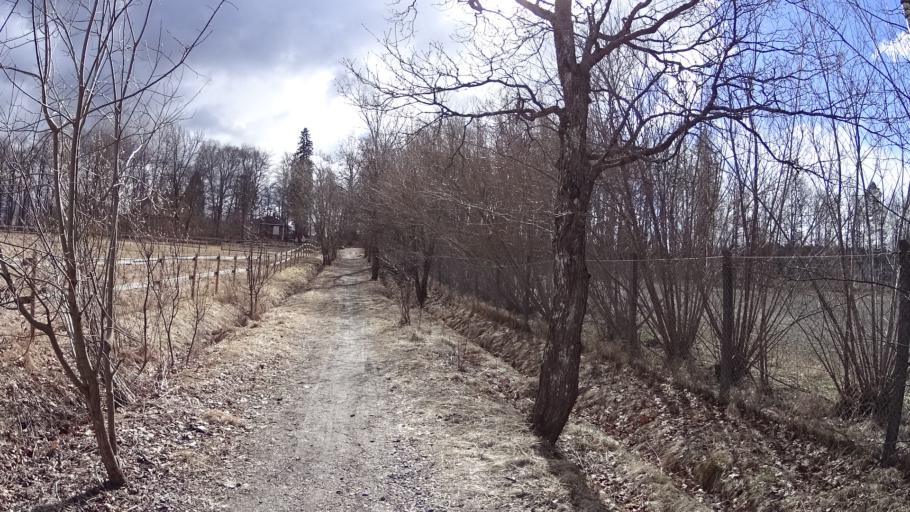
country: FI
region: Uusimaa
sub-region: Helsinki
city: Kauniainen
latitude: 60.2490
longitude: 24.6999
